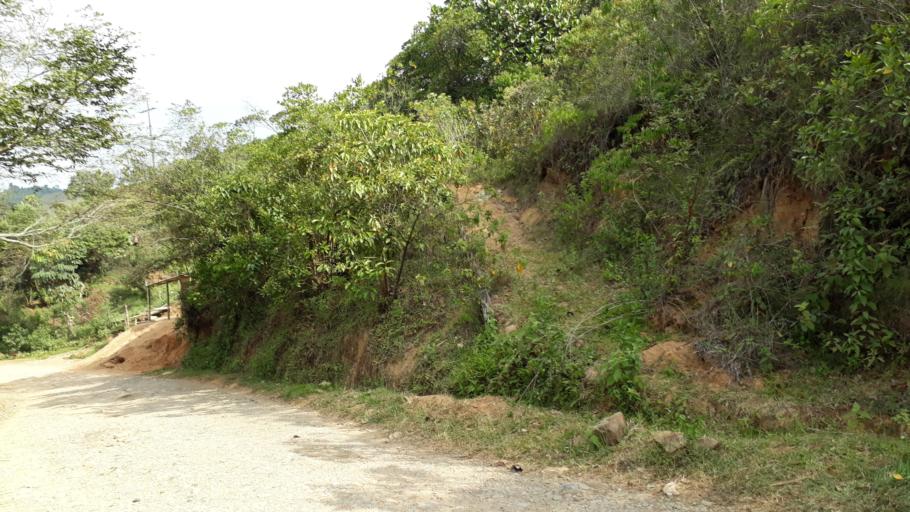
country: CO
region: Valle del Cauca
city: Jamundi
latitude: 3.2181
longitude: -76.6247
